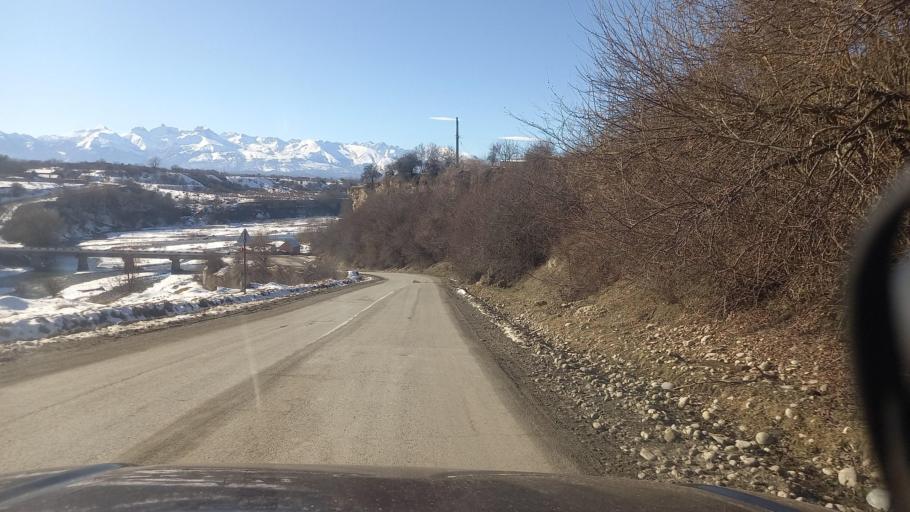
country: RU
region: North Ossetia
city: Chikola
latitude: 43.2317
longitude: 43.9333
